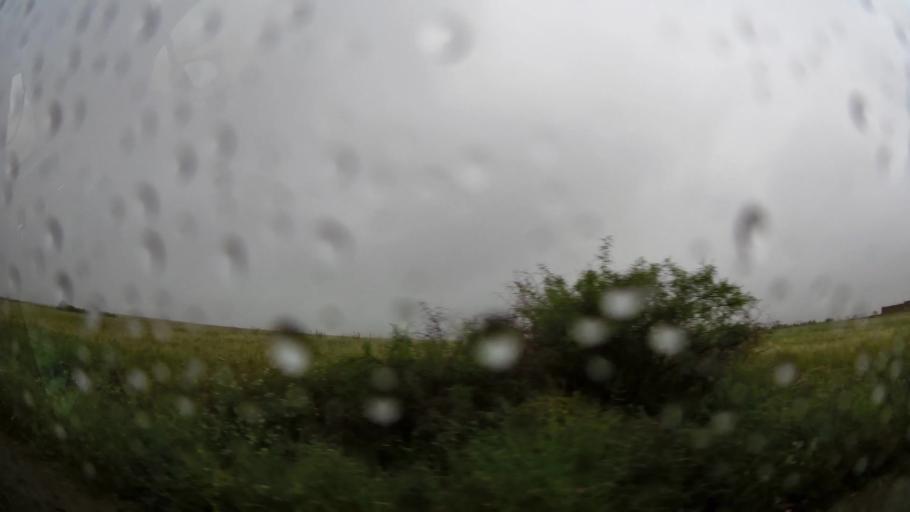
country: MA
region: Oriental
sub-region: Nador
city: Boudinar
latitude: 35.1284
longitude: -3.6470
